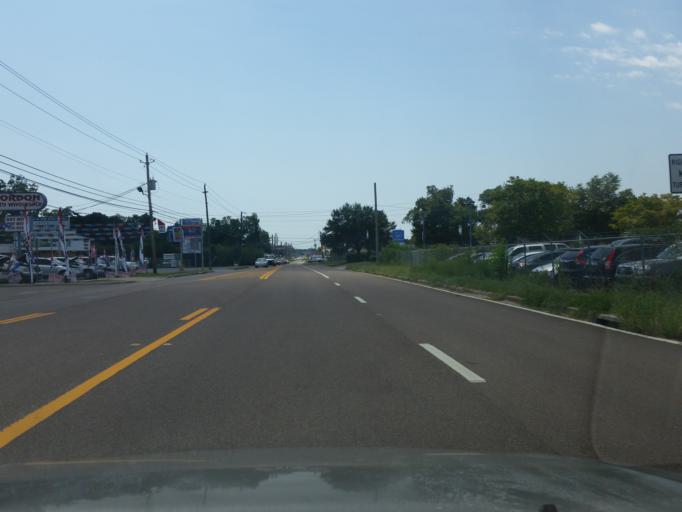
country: US
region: Florida
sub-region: Escambia County
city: Brent
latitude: 30.4739
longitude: -87.2450
